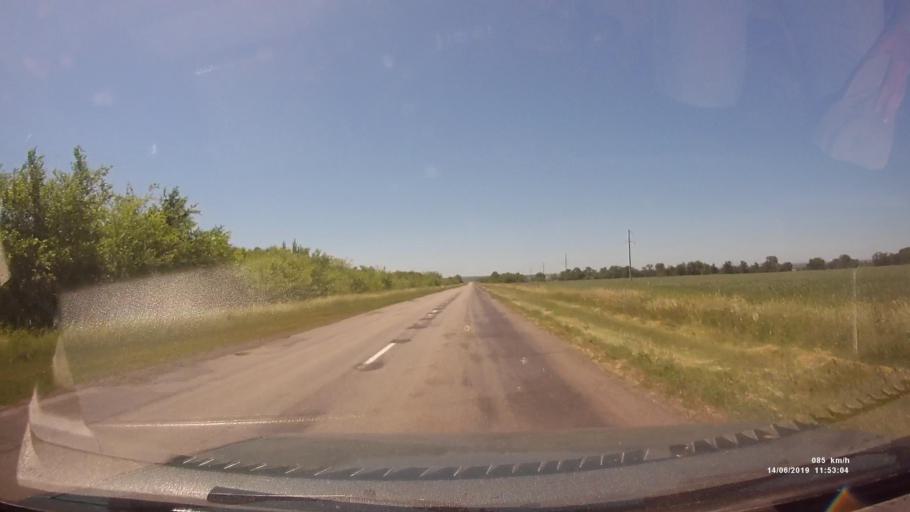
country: RU
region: Rostov
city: Kazanskaya
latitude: 49.8307
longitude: 41.2179
